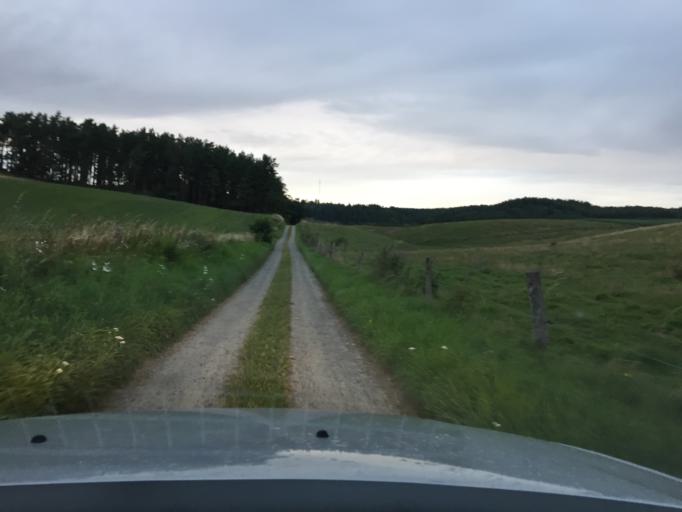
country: SE
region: Skane
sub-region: Kristianstads Kommun
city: Degeberga
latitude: 55.7219
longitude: 14.1271
